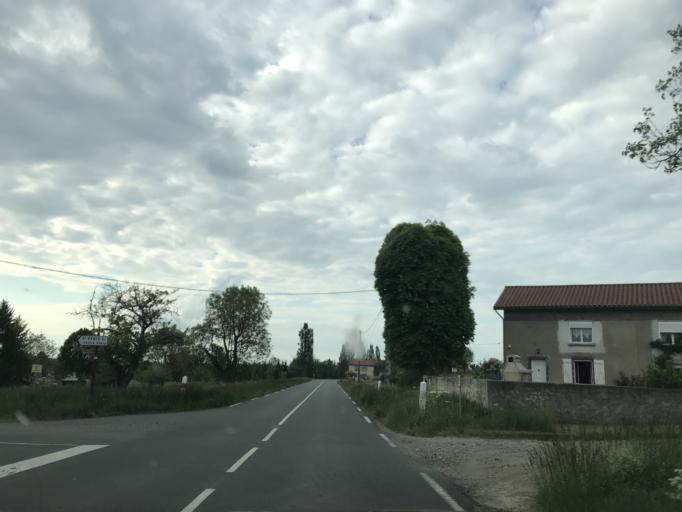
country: FR
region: Auvergne
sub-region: Departement du Puy-de-Dome
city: Maringues
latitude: 45.9627
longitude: 3.3376
